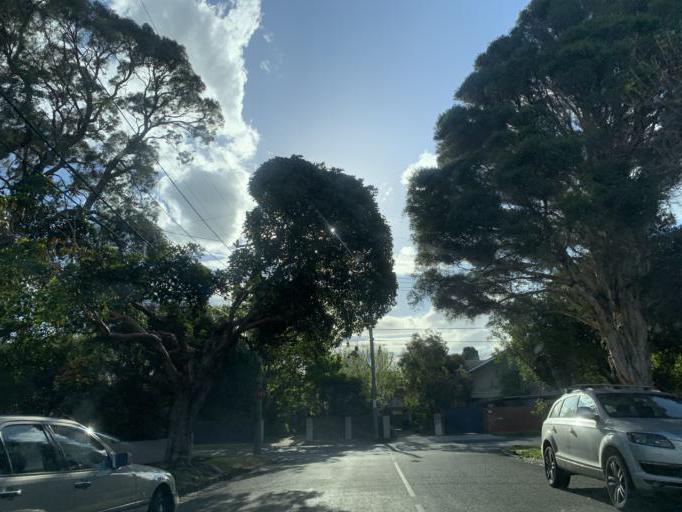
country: AU
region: Victoria
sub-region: Bayside
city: North Brighton
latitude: -37.9063
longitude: 144.9885
